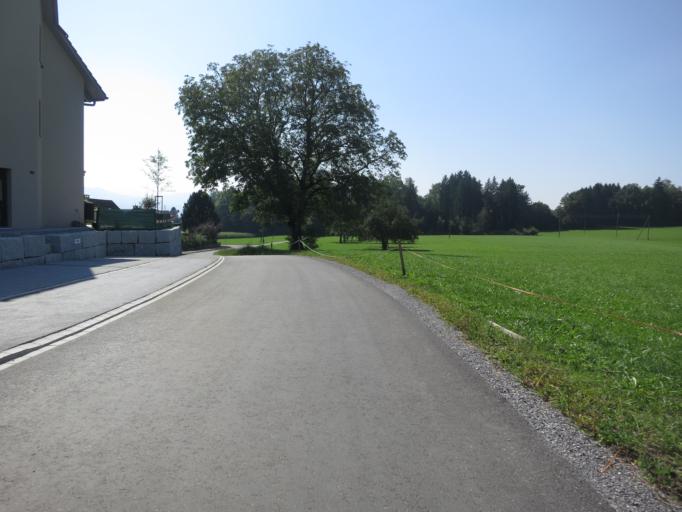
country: CH
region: Zurich
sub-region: Bezirk Hinwil
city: Wolfhausen
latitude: 47.2598
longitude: 8.7918
